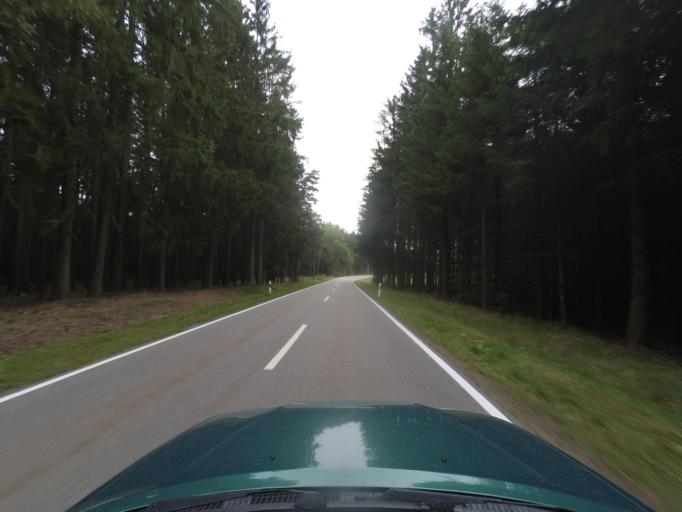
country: DE
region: Bavaria
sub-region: Upper Palatinate
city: Eslarn
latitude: 49.5863
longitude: 12.4813
